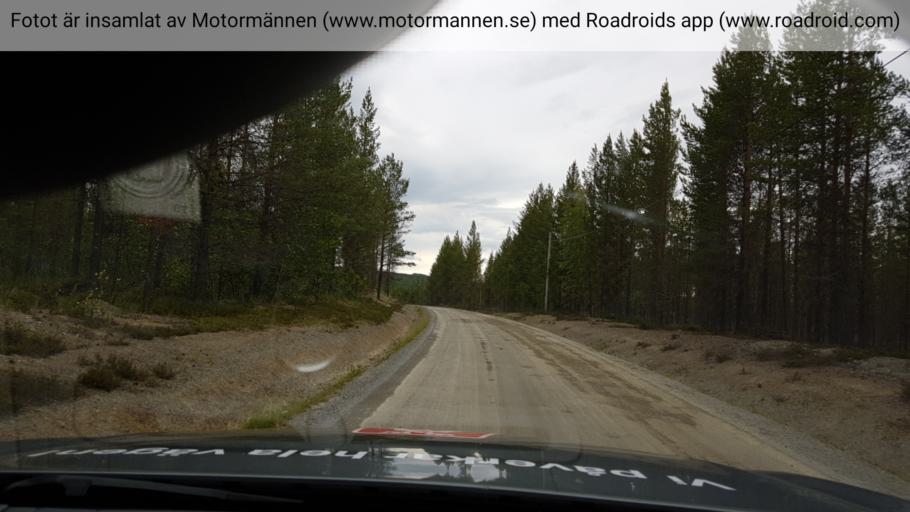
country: SE
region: Jaemtland
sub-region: Bergs Kommun
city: Hoverberg
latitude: 62.7631
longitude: 13.8230
